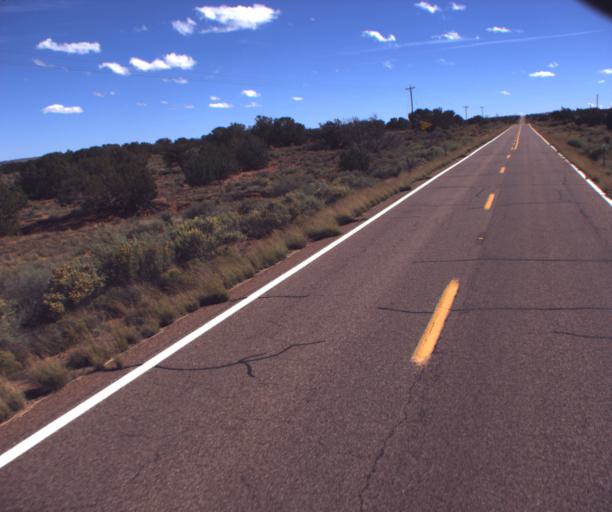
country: US
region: Arizona
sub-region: Apache County
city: Saint Johns
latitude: 34.6036
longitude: -109.6539
